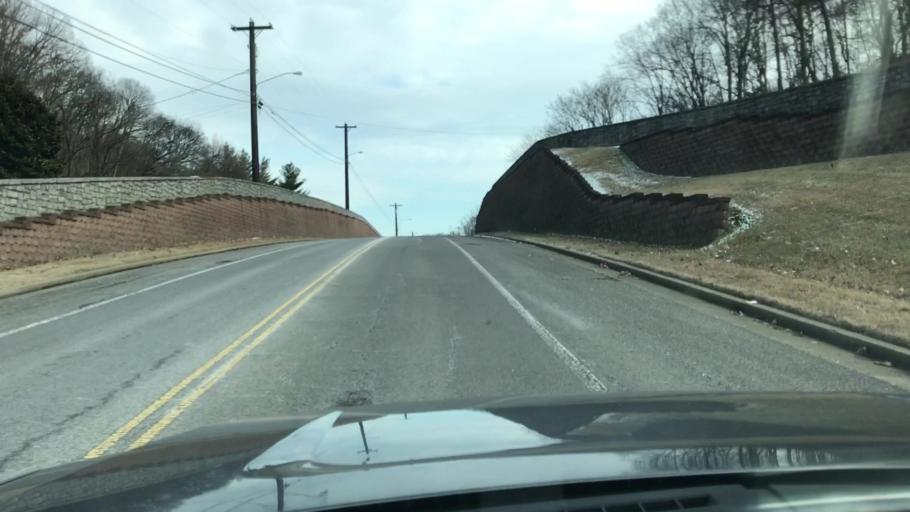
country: US
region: Tennessee
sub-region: Williamson County
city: Brentwood
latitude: 36.0127
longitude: -86.8315
